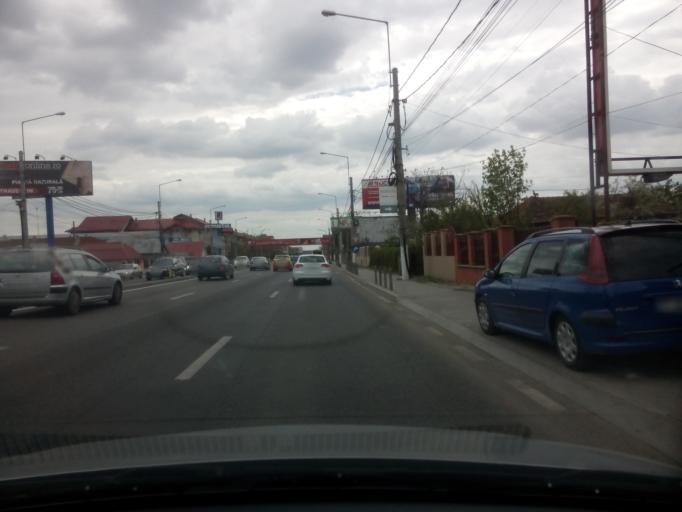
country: RO
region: Ilfov
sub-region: Comuna Otopeni
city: Otopeni
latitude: 44.5559
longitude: 26.0691
